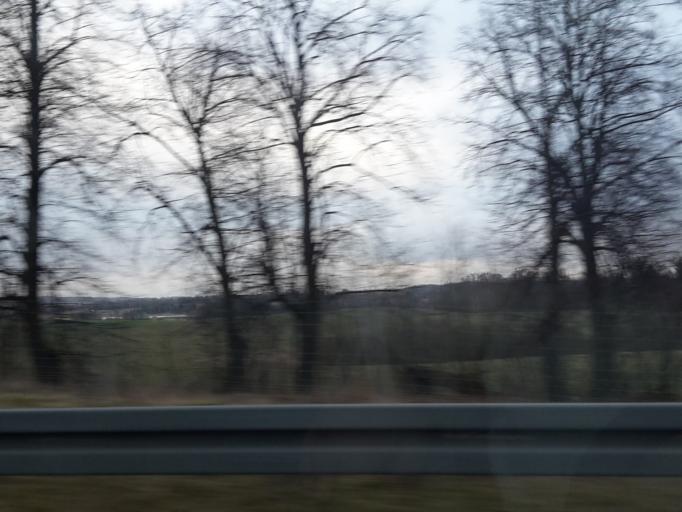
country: PL
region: Warmian-Masurian Voivodeship
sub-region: Powiat ostrodzki
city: Maldyty
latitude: 53.9334
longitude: 19.7059
